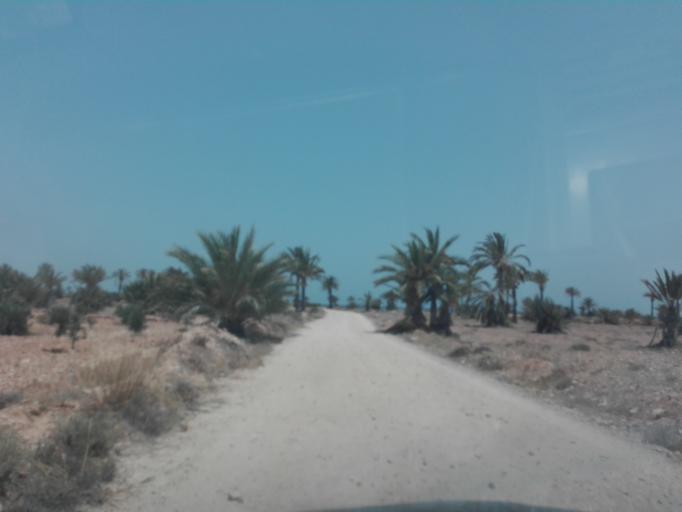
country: TN
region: Safaqis
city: Al Qarmadah
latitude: 34.6656
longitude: 11.0928
